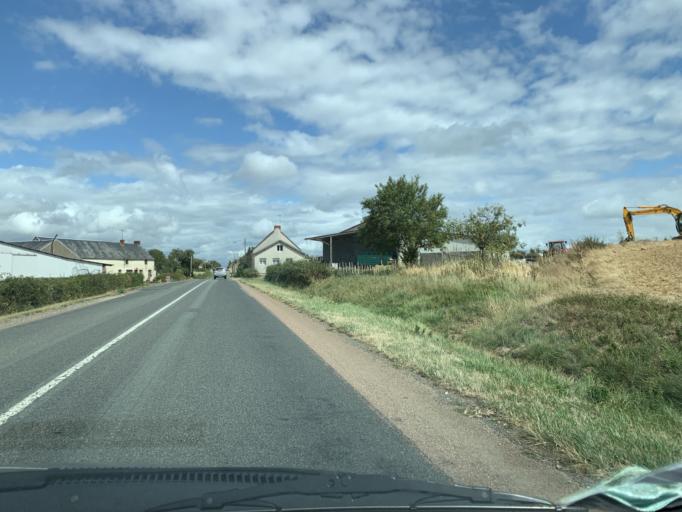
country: FR
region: Bourgogne
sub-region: Departement de la Nievre
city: Varzy
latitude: 47.3737
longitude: 3.4256
